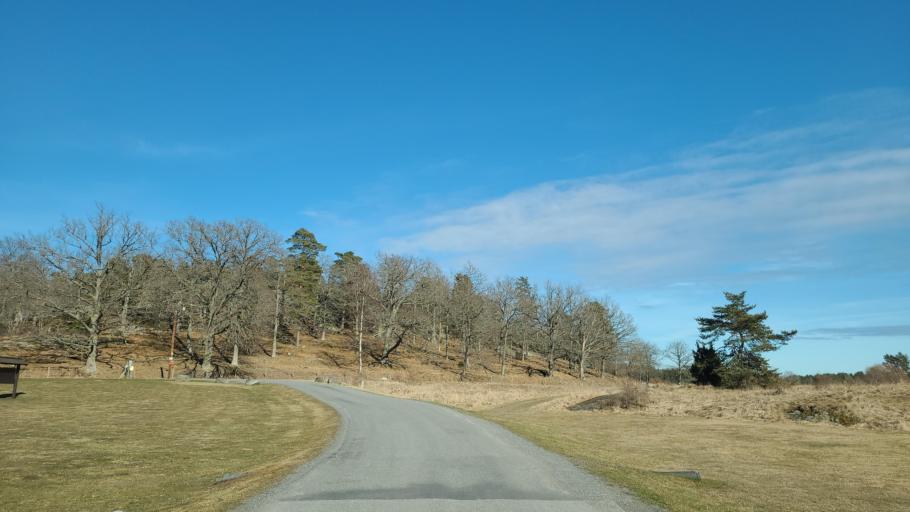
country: SE
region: Stockholm
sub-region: Varmdo Kommun
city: Hemmesta
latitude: 59.2749
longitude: 18.5468
